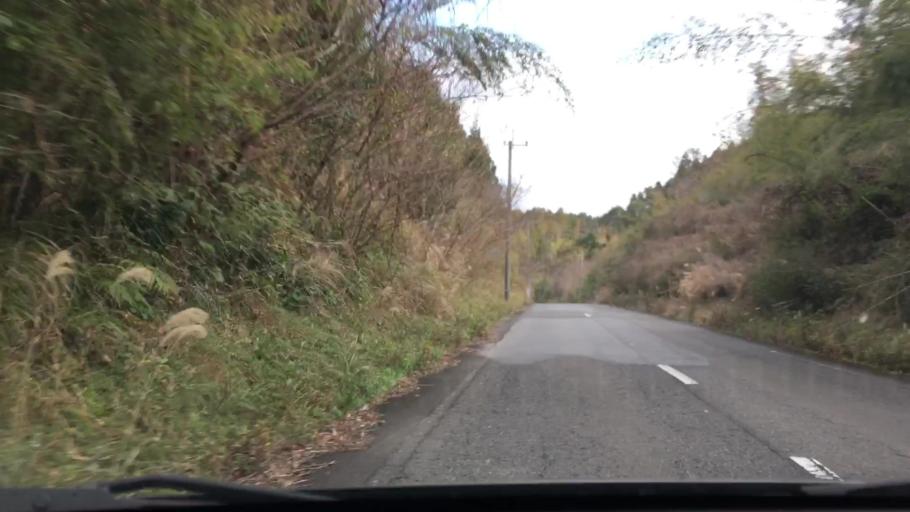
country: JP
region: Miyazaki
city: Nichinan
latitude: 31.6098
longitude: 131.3322
